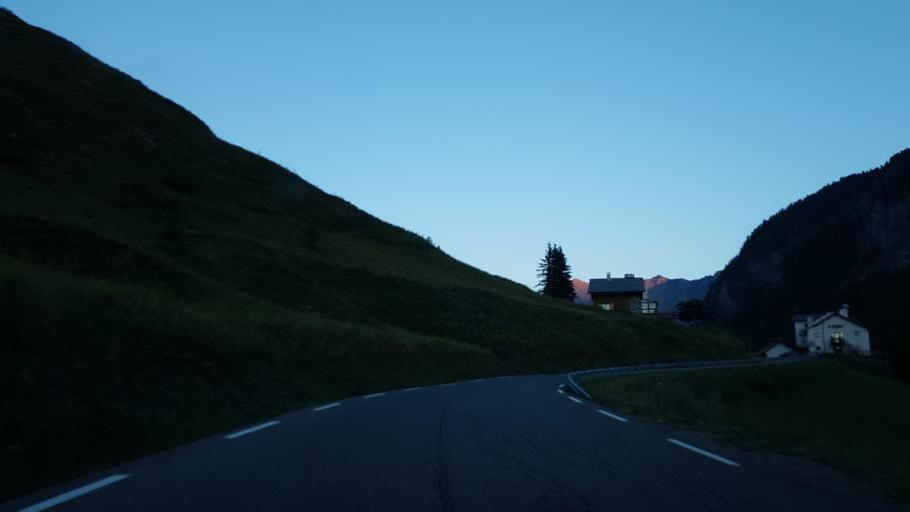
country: IT
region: Piedmont
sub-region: Provincia di Cuneo
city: Pontechianale
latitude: 44.7027
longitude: 6.8579
